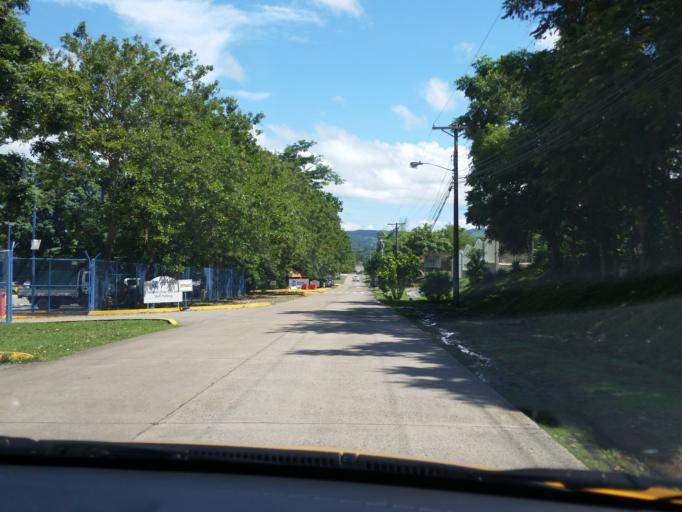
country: PA
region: Panama
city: San Miguelito
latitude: 9.0764
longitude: -79.4702
